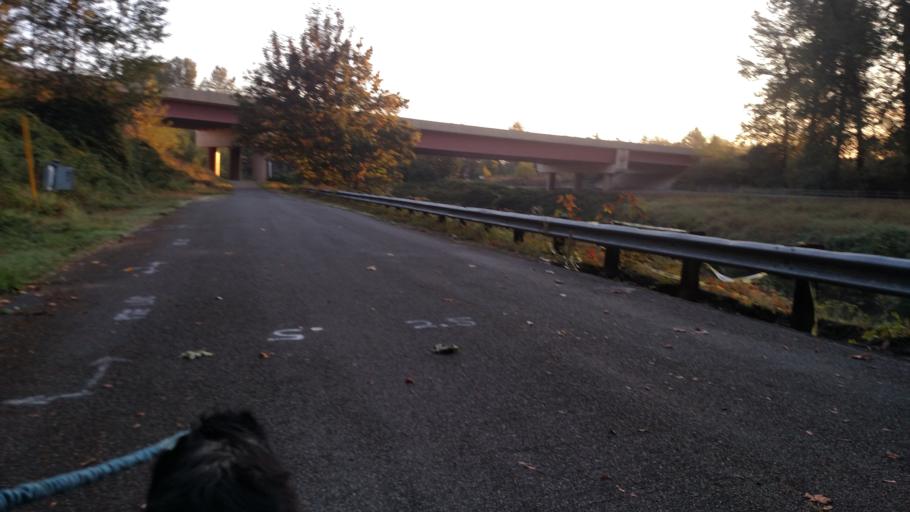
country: US
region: Washington
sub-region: King County
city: Kent
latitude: 47.3951
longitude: -122.2746
